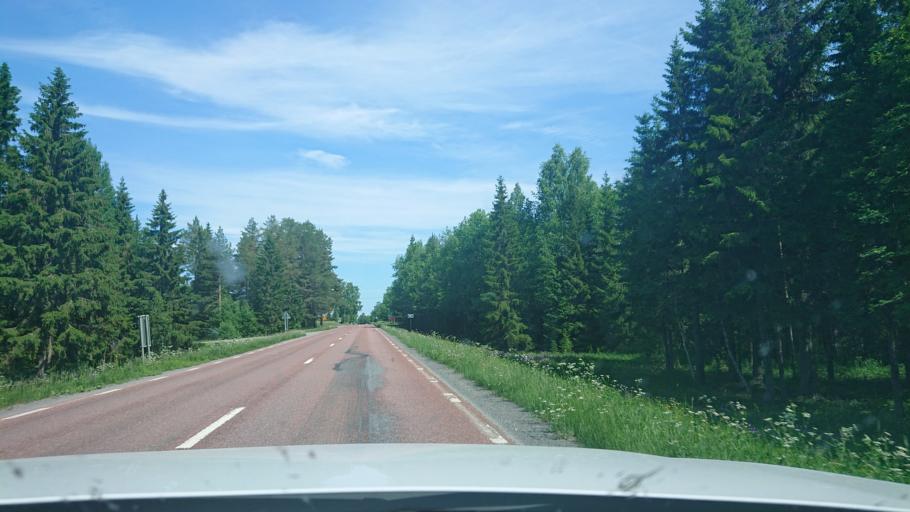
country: SE
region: Jaemtland
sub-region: Stroemsunds Kommun
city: Stroemsund
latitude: 63.7263
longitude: 15.4811
